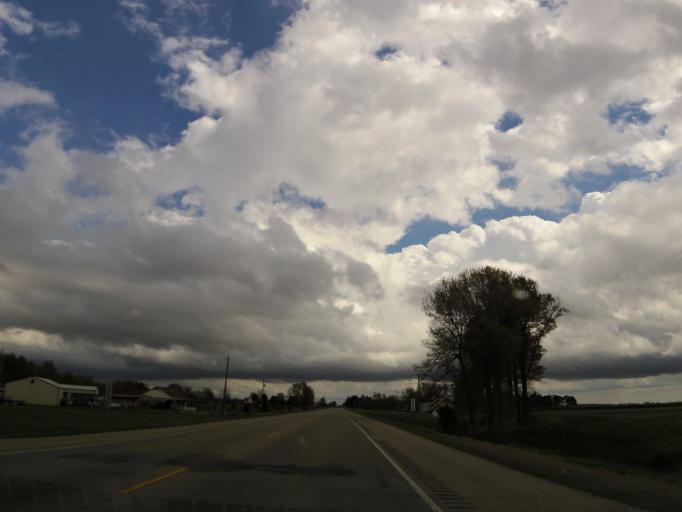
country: US
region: Arkansas
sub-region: Clay County
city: Corning
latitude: 36.4588
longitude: -90.5794
